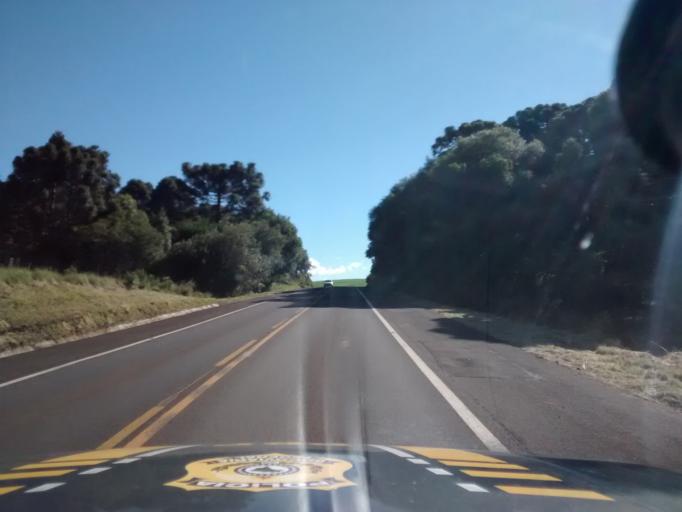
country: BR
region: Rio Grande do Sul
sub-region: Lagoa Vermelha
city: Lagoa Vermelha
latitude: -28.3297
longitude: -51.2836
